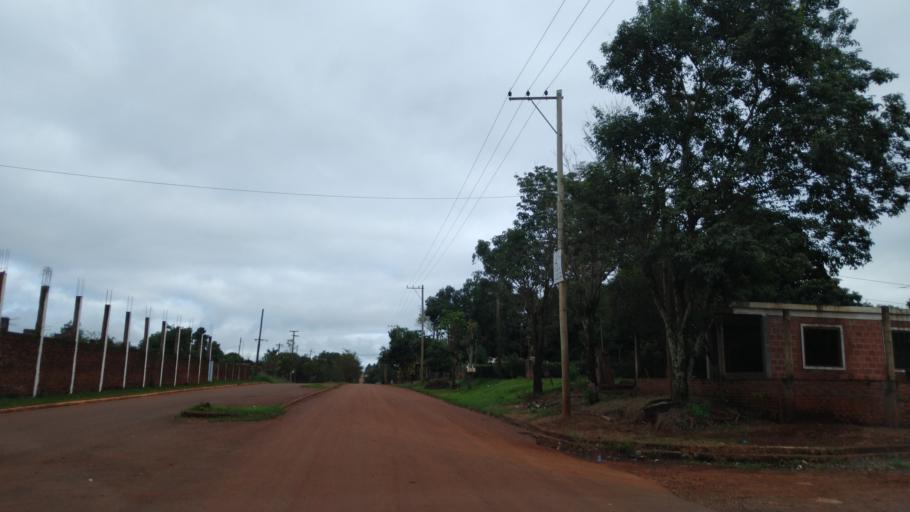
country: AR
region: Misiones
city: Jardin America
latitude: -27.0314
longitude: -55.2350
